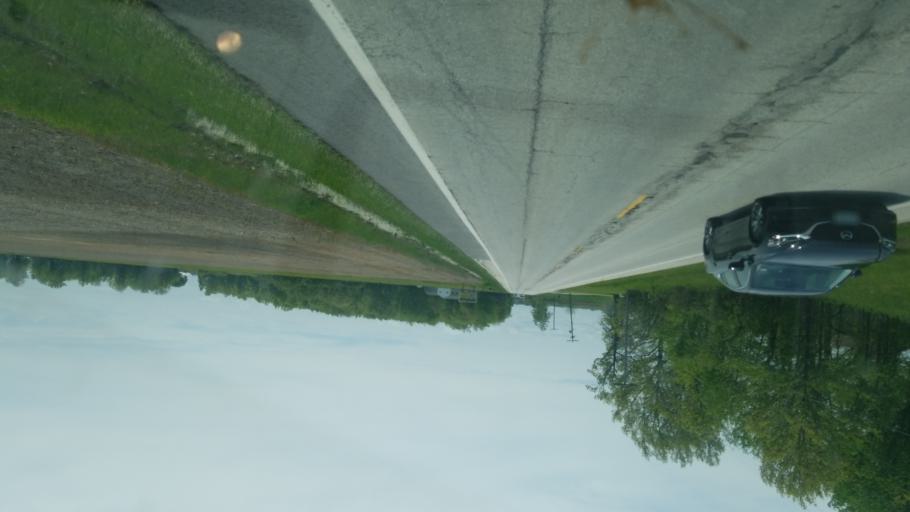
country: US
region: Ohio
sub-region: Ottawa County
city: Oak Harbor
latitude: 41.5511
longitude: -83.0603
